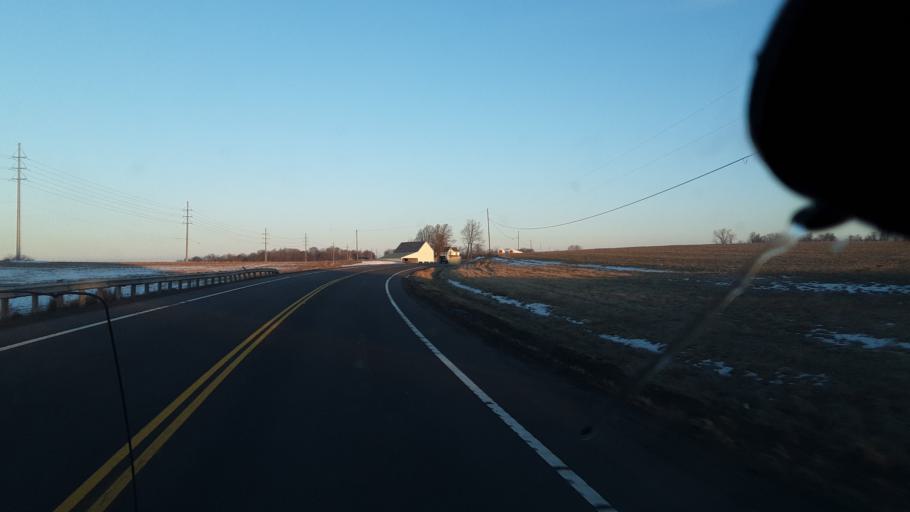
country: US
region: Ohio
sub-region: Perry County
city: Somerset
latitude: 39.8150
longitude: -82.3176
